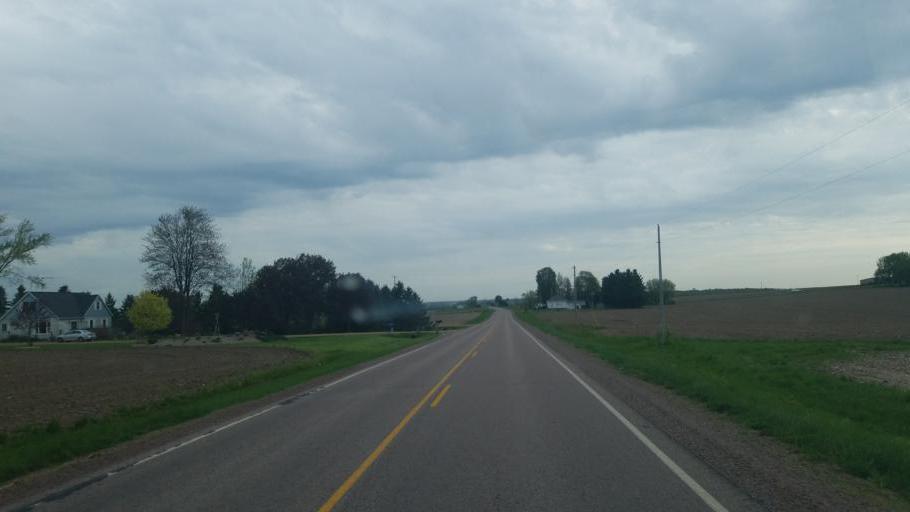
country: US
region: Wisconsin
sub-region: Wood County
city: Marshfield
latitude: 44.5943
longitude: -90.2988
